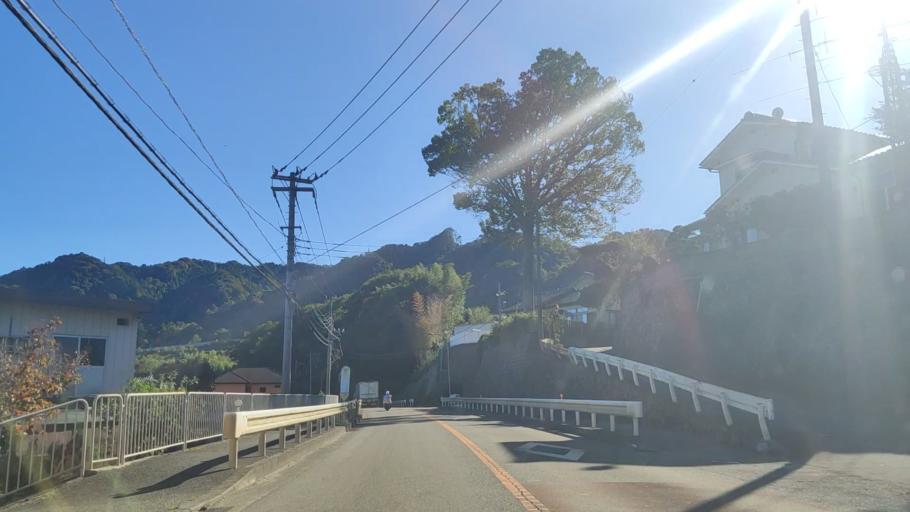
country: JP
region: Tokyo
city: Hachioji
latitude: 35.5825
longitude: 139.2981
